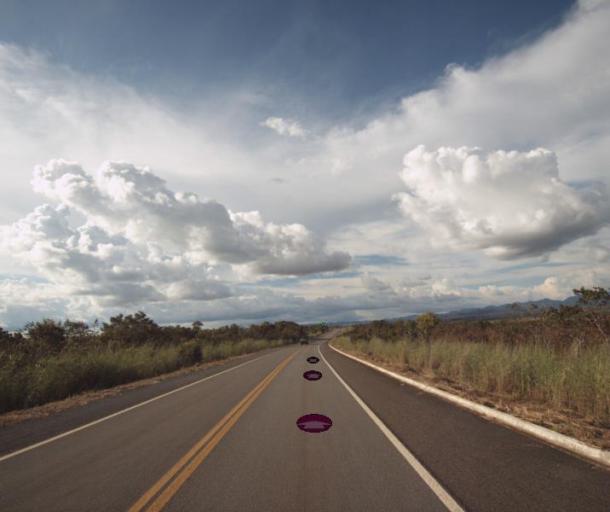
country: BR
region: Goias
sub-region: Barro Alto
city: Barro Alto
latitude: -14.8239
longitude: -48.6383
